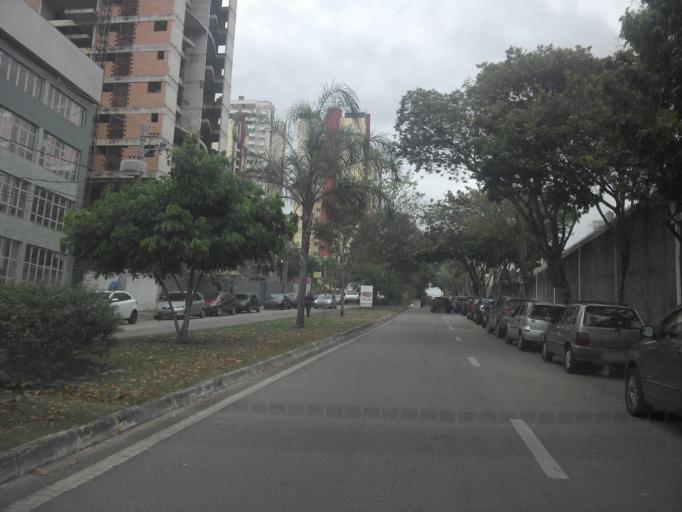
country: BR
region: Sao Paulo
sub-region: Sao Jose Dos Campos
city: Sao Jose dos Campos
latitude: -23.2161
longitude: -45.9030
